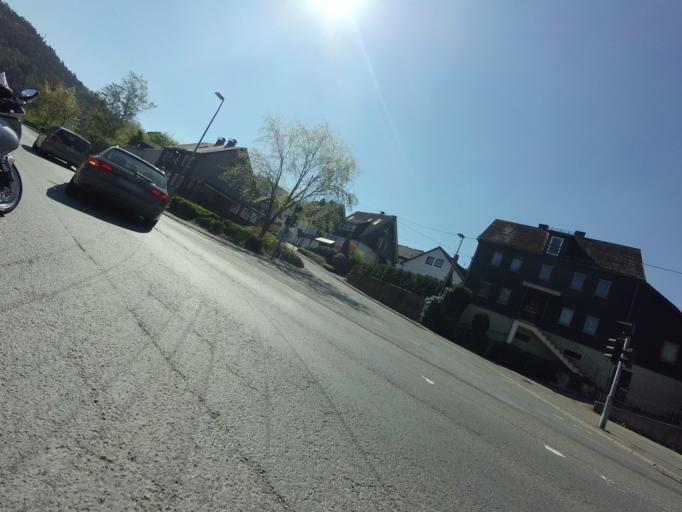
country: DE
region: North Rhine-Westphalia
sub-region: Regierungsbezirk Arnsberg
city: Lennestadt
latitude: 51.1094
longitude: 8.0682
